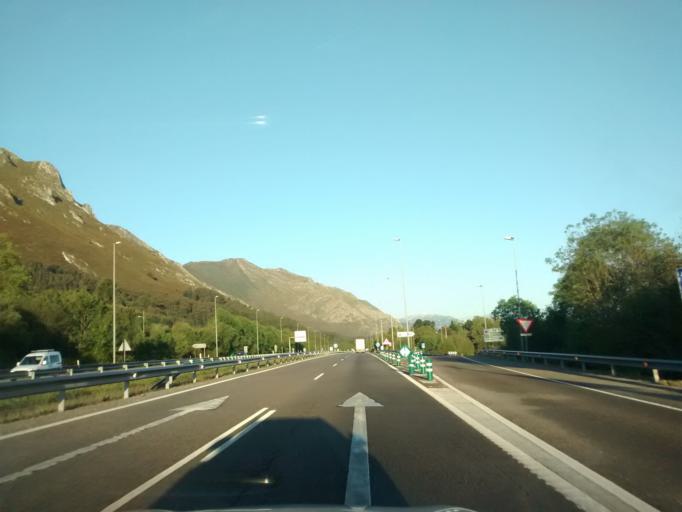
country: ES
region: Asturias
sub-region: Province of Asturias
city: Ribadesella
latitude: 43.4400
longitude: -4.9589
